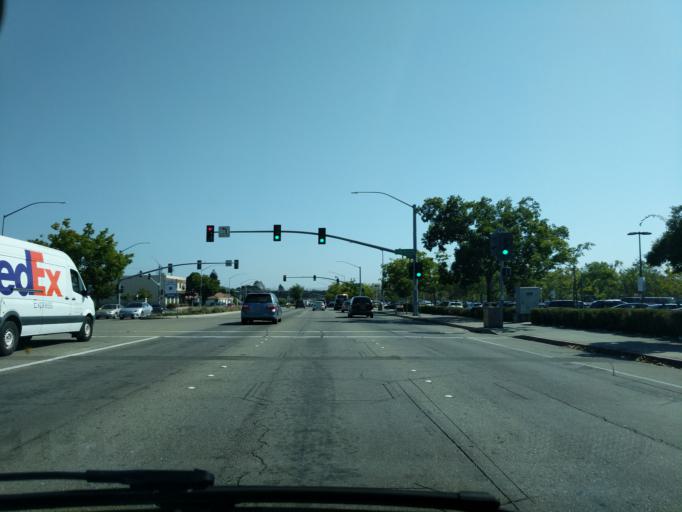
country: US
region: California
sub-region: Alameda County
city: Castro Valley
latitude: 37.6935
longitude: -122.0740
